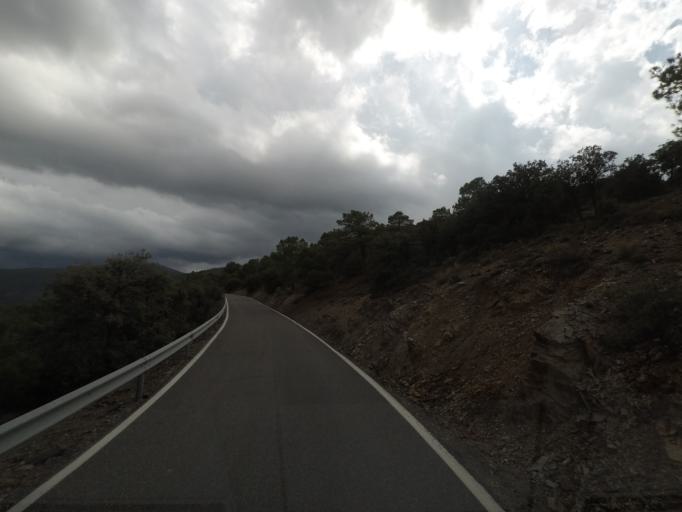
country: ES
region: Andalusia
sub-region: Provincia de Granada
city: Aldeire
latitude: 37.1565
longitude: -3.0505
